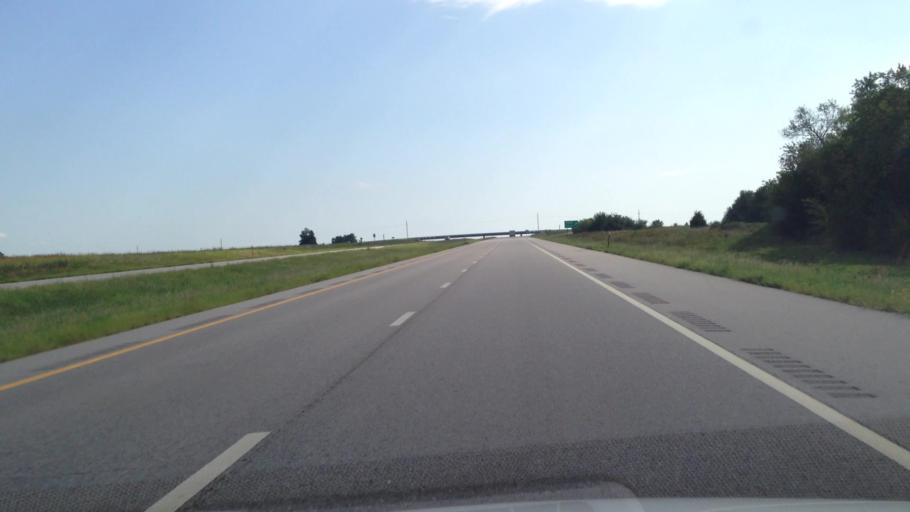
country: US
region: Kansas
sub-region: Linn County
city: La Cygne
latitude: 38.4098
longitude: -94.6879
